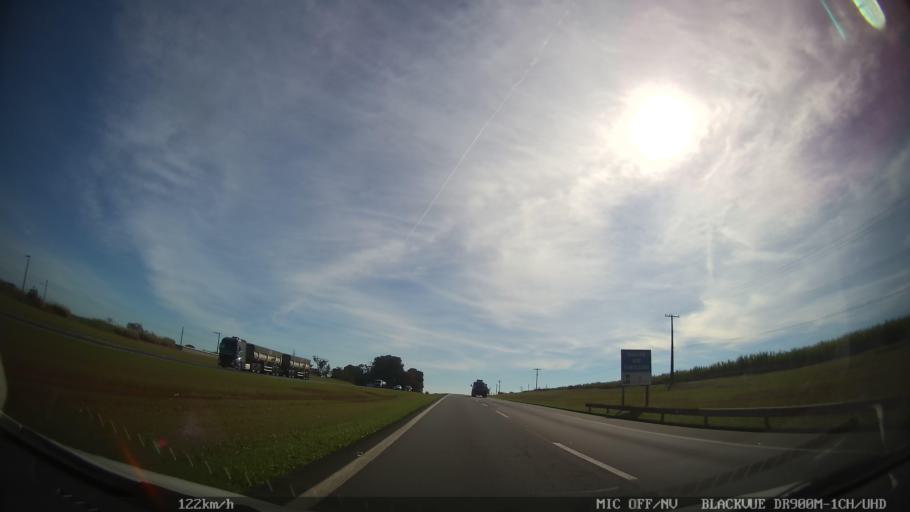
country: BR
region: Sao Paulo
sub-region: Cordeiropolis
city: Cordeiropolis
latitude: -22.4650
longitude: -47.3989
